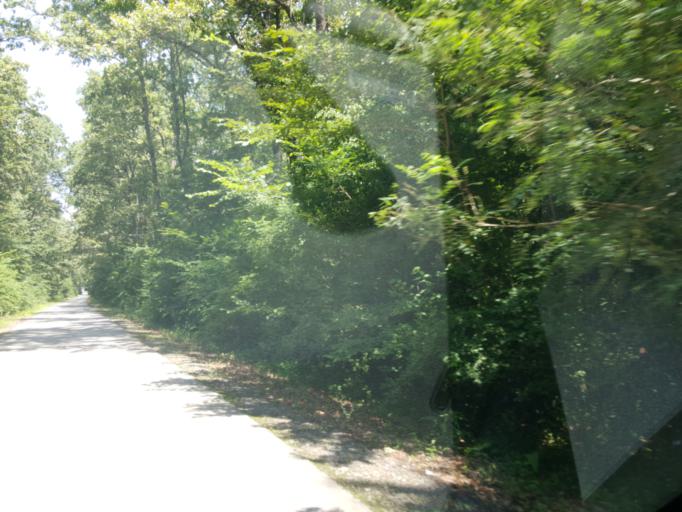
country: RS
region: Autonomna Pokrajina Vojvodina
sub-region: Sremski Okrug
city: Sid
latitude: 45.0388
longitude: 19.1383
